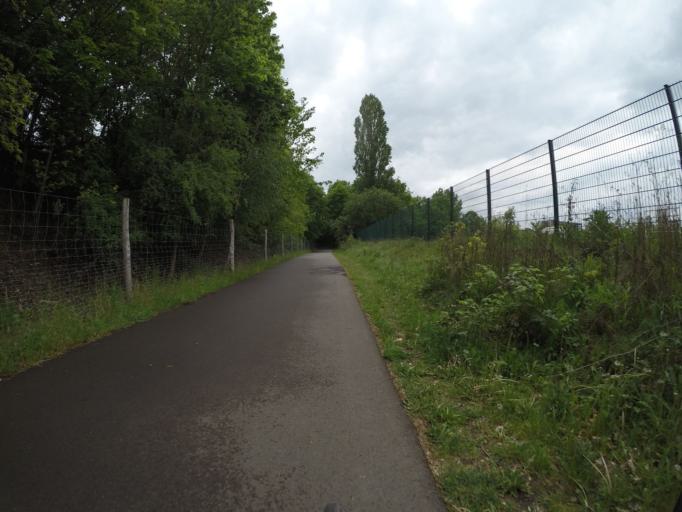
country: DE
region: Berlin
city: Lichtenberg
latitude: 52.5298
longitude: 13.5032
